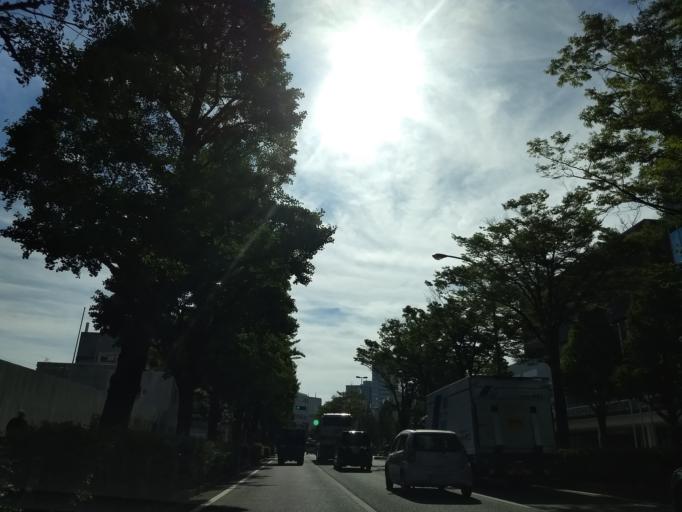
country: JP
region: Kanagawa
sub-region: Kawasaki-shi
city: Kawasaki
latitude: 35.5292
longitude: 139.7095
